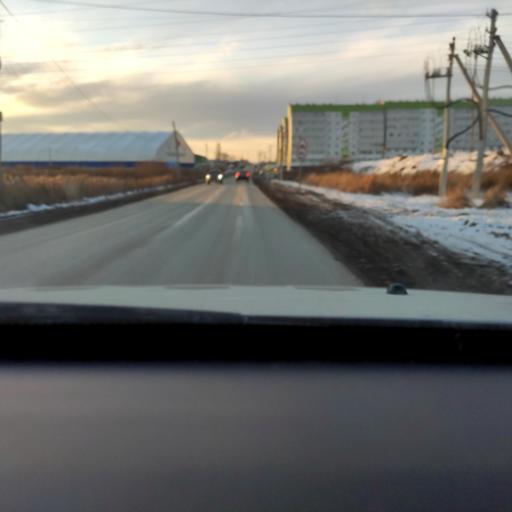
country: RU
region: Perm
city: Froly
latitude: 57.9195
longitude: 56.2877
